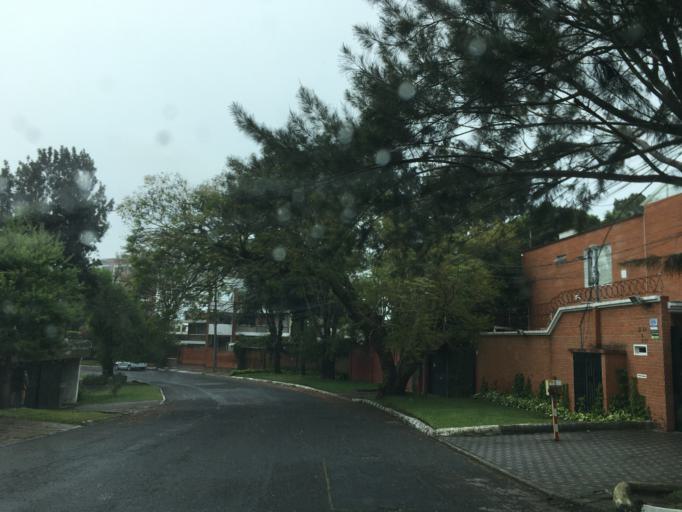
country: GT
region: Guatemala
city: Santa Catarina Pinula
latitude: 14.5849
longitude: -90.4899
